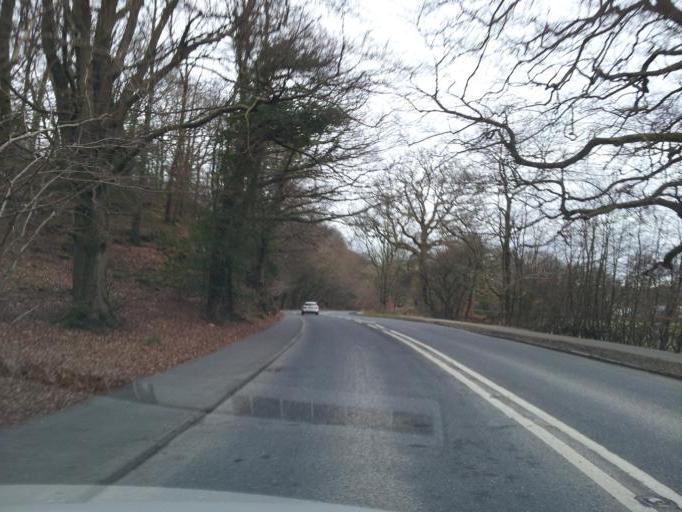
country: GB
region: England
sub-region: Cumbria
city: Windermere
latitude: 54.3774
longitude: -2.9195
